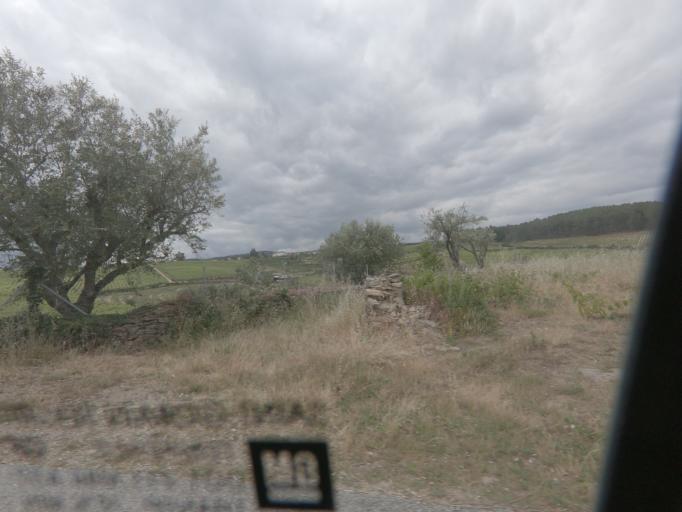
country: PT
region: Vila Real
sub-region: Sabrosa
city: Sabrosa
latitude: 41.2555
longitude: -7.5857
